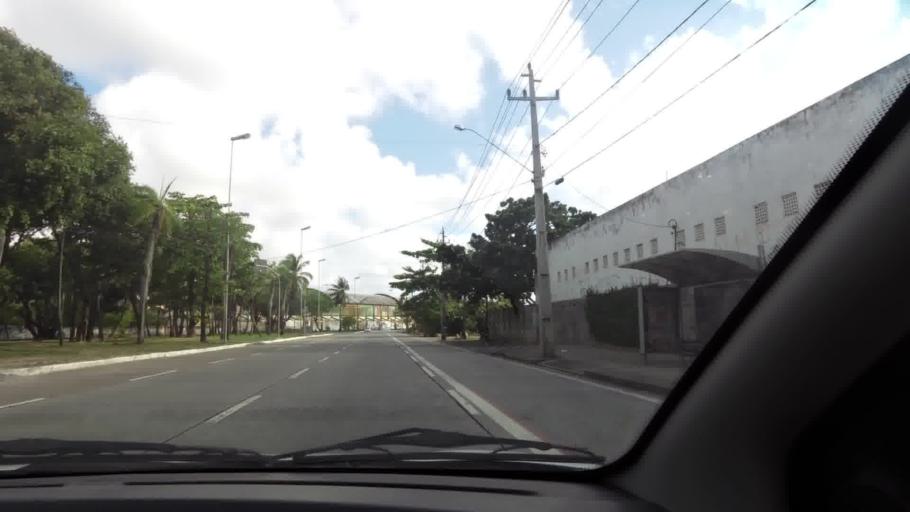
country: BR
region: Pernambuco
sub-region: Recife
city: Recife
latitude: -8.0784
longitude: -34.8915
